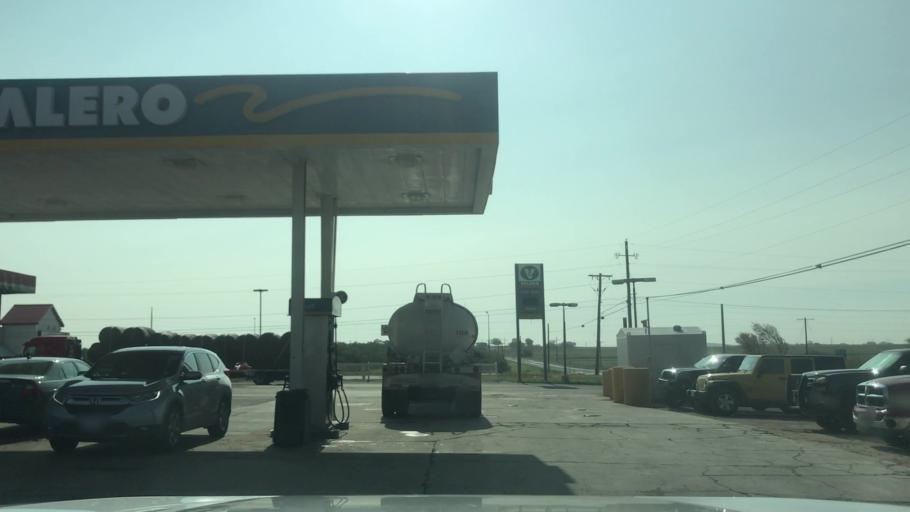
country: US
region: Texas
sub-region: Scurry County
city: Snyder
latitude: 32.7050
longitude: -100.8661
